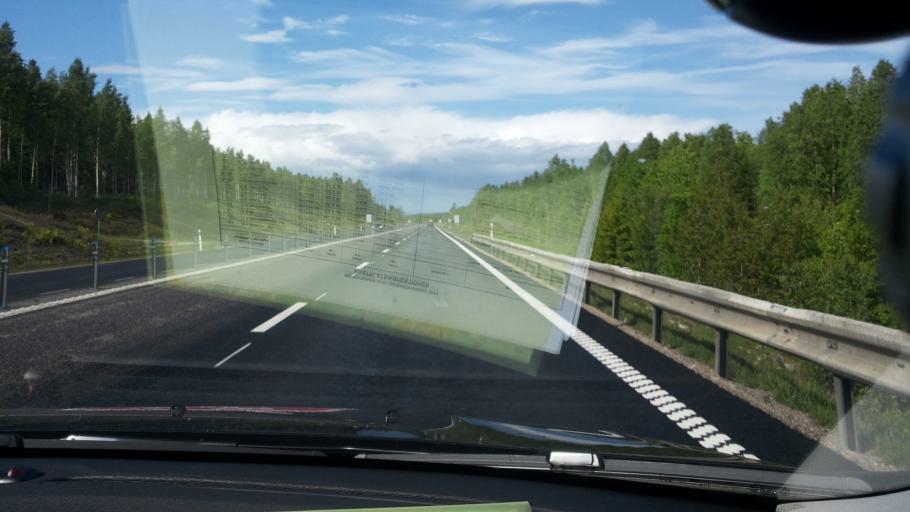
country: SE
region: Vaesternorrland
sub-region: Sundsvalls Kommun
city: Njurundabommen
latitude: 62.1977
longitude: 17.3706
